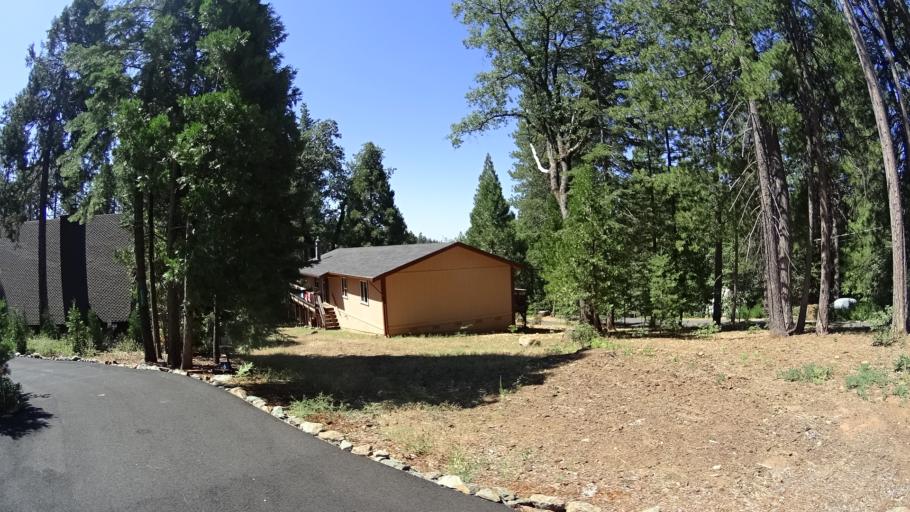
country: US
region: California
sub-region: Calaveras County
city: Arnold
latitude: 38.2376
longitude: -120.3748
